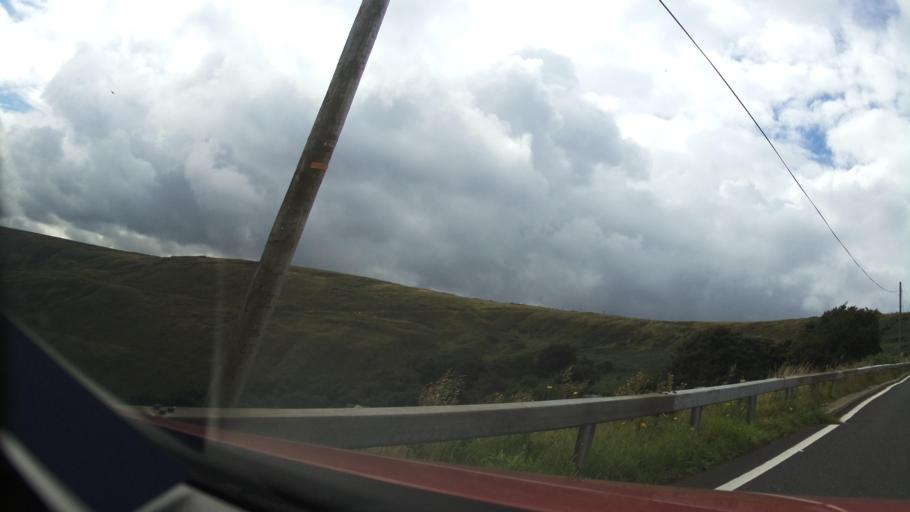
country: GB
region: England
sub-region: Kirklees
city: Meltham
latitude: 53.5365
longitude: -1.8522
